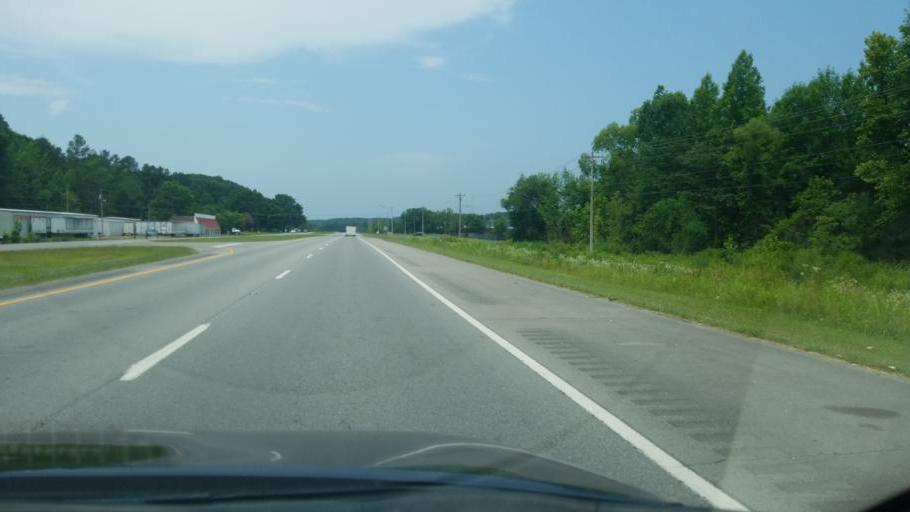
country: US
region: Tennessee
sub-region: Humphreys County
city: Waverly
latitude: 36.0767
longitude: -87.8557
